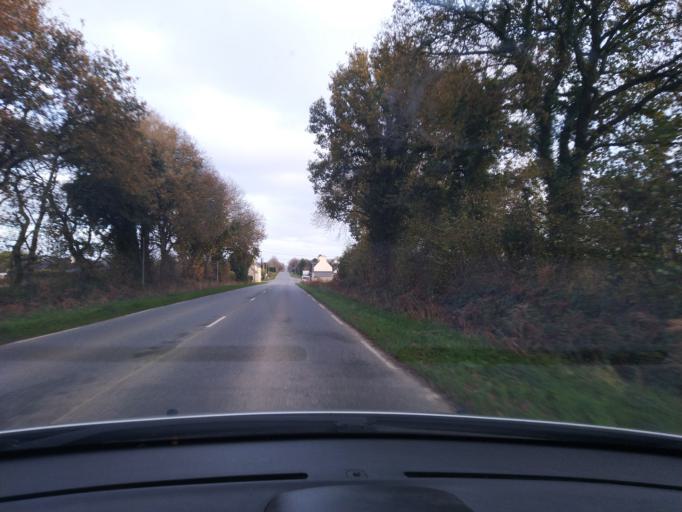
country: FR
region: Brittany
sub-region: Departement du Finistere
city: Plourin-les-Morlaix
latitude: 48.5748
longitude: -3.7568
